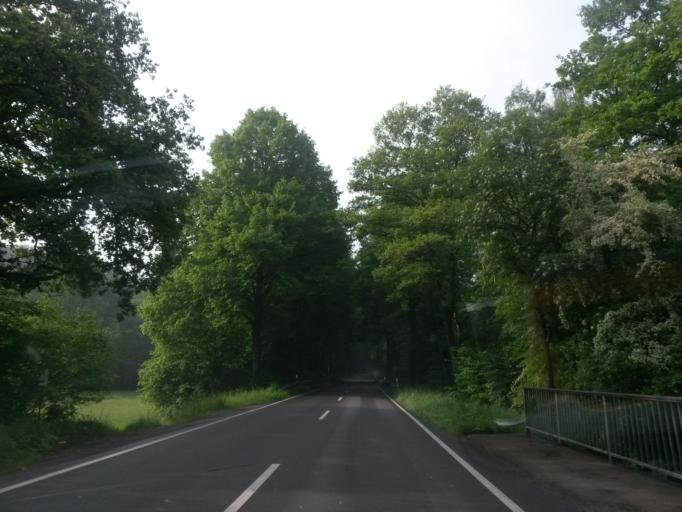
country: DE
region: North Rhine-Westphalia
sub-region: Regierungsbezirk Koln
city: Hennef
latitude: 50.8483
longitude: 7.3197
